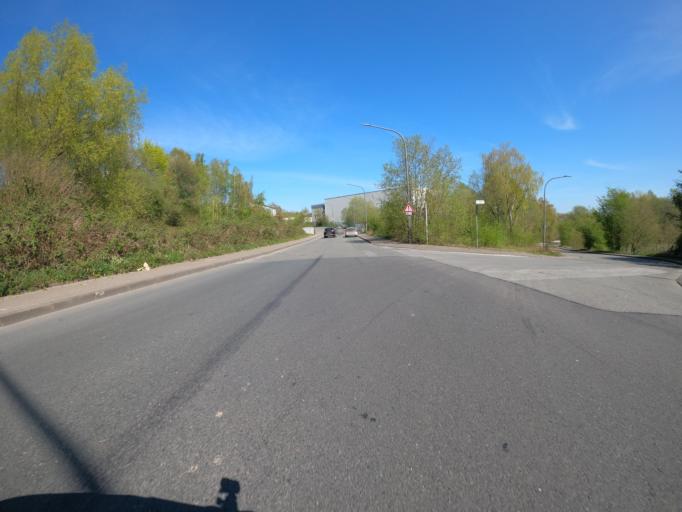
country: DE
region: North Rhine-Westphalia
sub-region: Regierungsbezirk Dusseldorf
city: Remscheid
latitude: 51.2359
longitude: 7.2246
